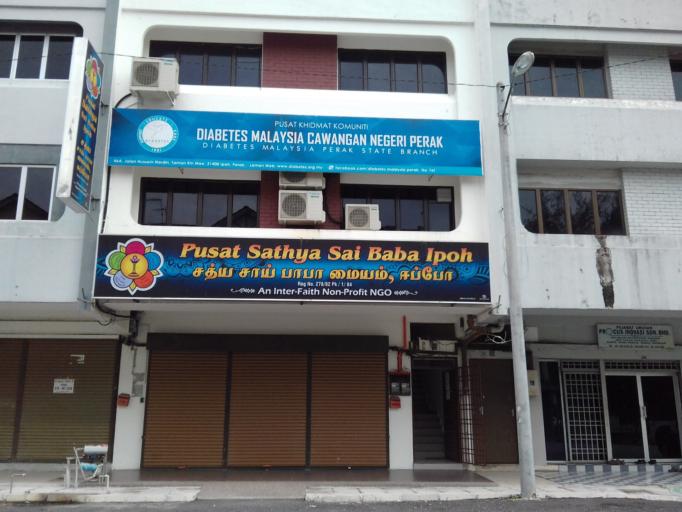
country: MY
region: Perak
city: Ipoh
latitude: 4.6107
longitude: 101.1002
